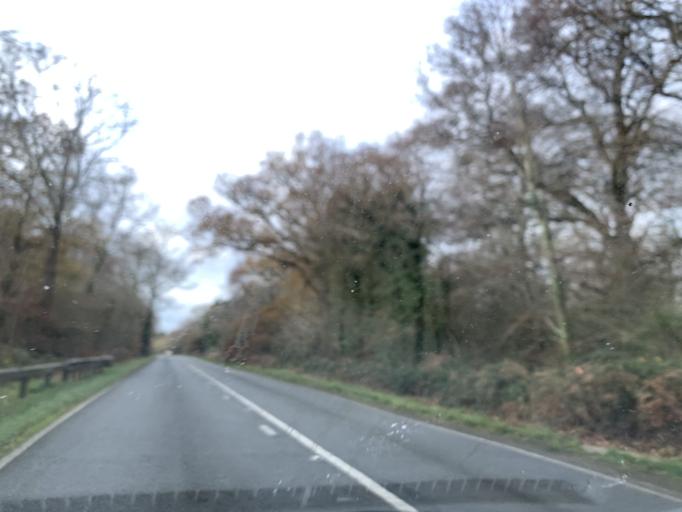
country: GB
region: England
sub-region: Hampshire
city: Lyndhurst
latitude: 50.8580
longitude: -1.6089
